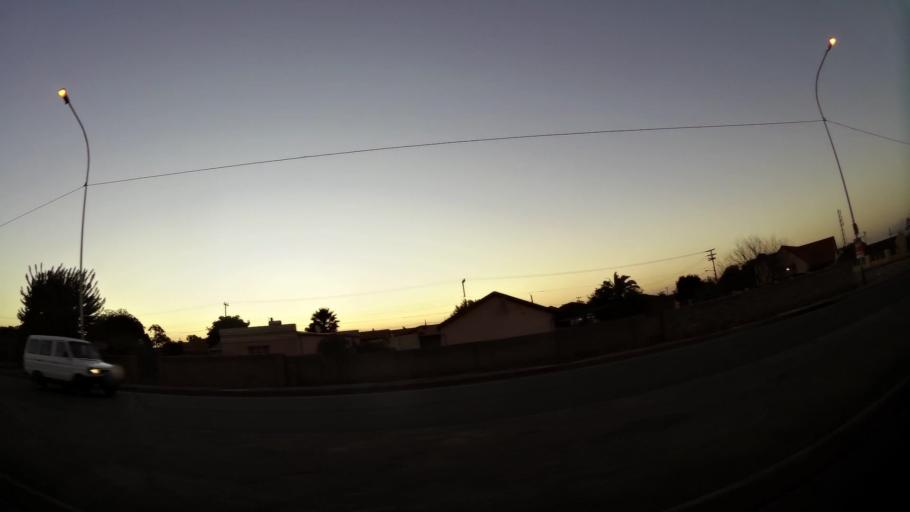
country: ZA
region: North-West
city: Ga-Rankuwa
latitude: -25.5977
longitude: 27.9765
